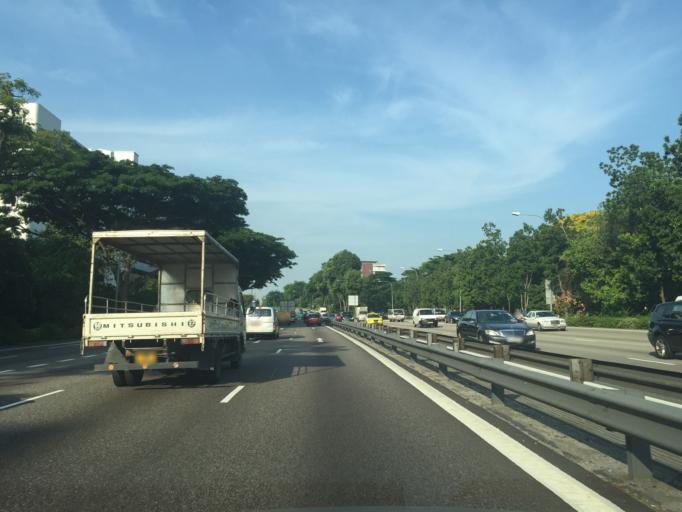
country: SG
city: Singapore
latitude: 1.3223
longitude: 103.8868
